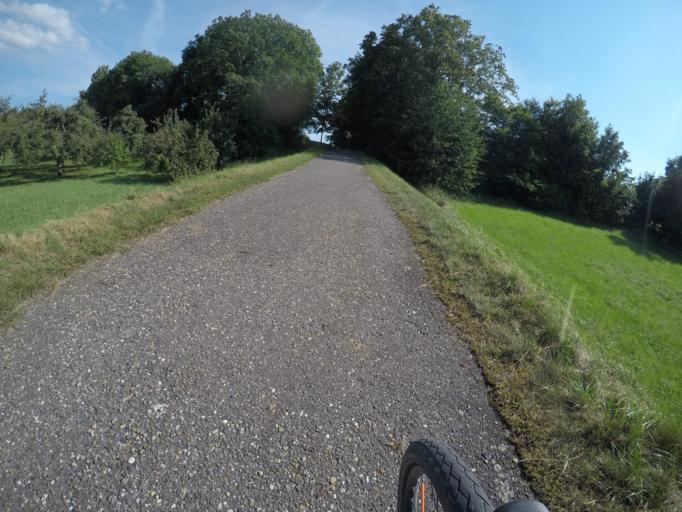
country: DE
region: Baden-Wuerttemberg
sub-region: Karlsruhe Region
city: Olbronn-Durrn
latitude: 48.9587
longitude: 8.7561
